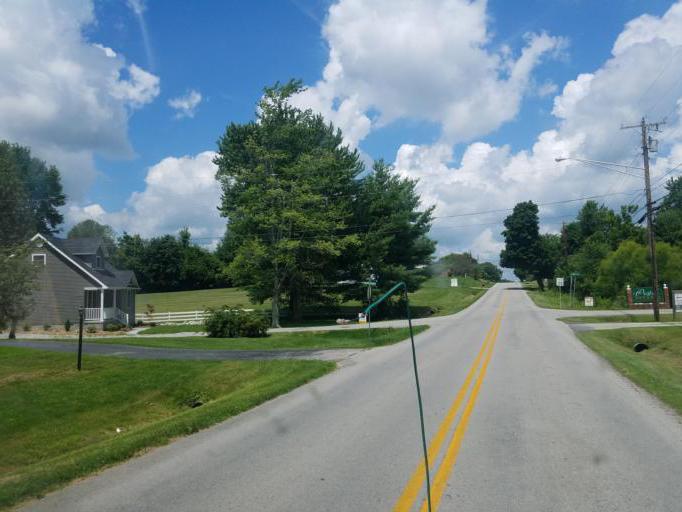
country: US
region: Kentucky
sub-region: Grayson County
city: Leitchfield
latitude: 37.4919
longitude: -86.2971
